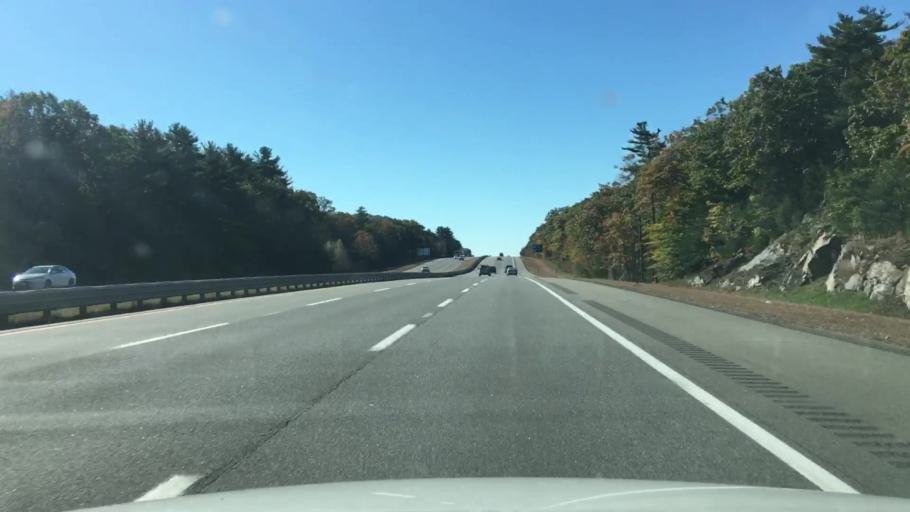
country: US
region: Maine
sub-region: York County
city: Cape Neddick
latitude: 43.1856
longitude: -70.6469
